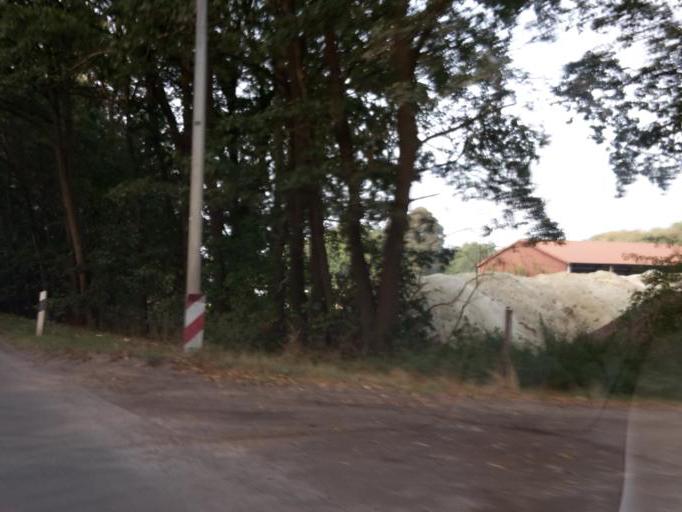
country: DE
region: Lower Saxony
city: Oldenburg
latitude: 53.1167
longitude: 8.2610
